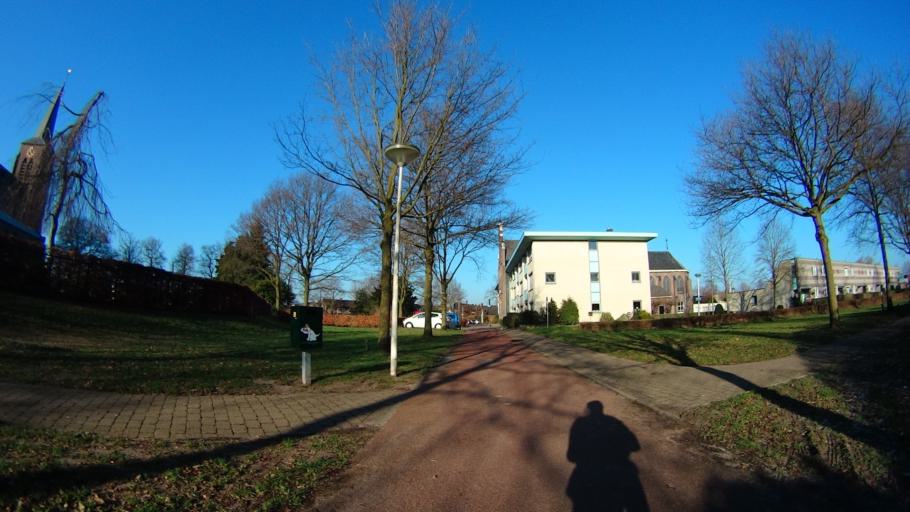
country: NL
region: Utrecht
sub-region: Gemeente Amersfoort
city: Hoogland
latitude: 52.1906
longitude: 5.3852
